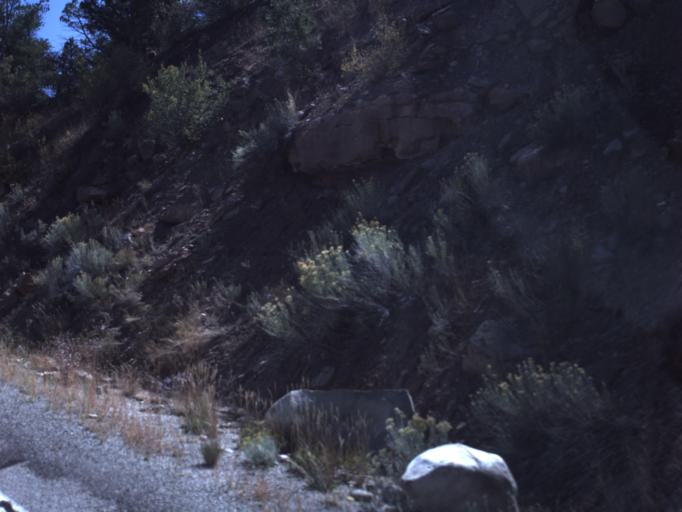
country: US
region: Utah
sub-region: Grand County
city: Moab
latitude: 38.3291
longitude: -109.0945
